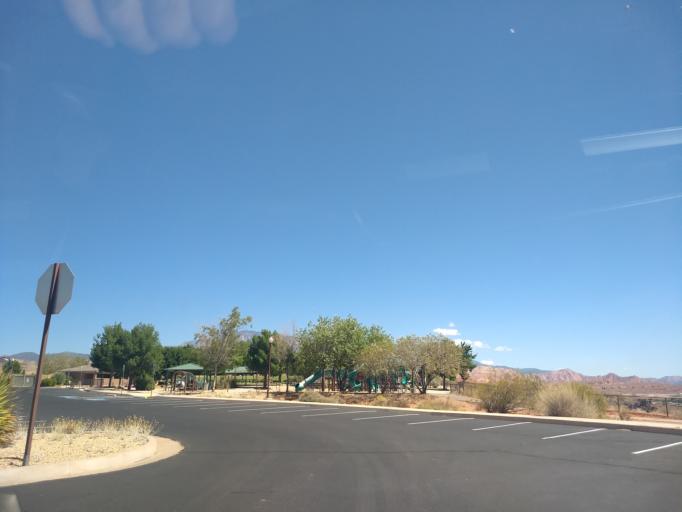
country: US
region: Utah
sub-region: Washington County
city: Washington
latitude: 37.1474
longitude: -113.4647
